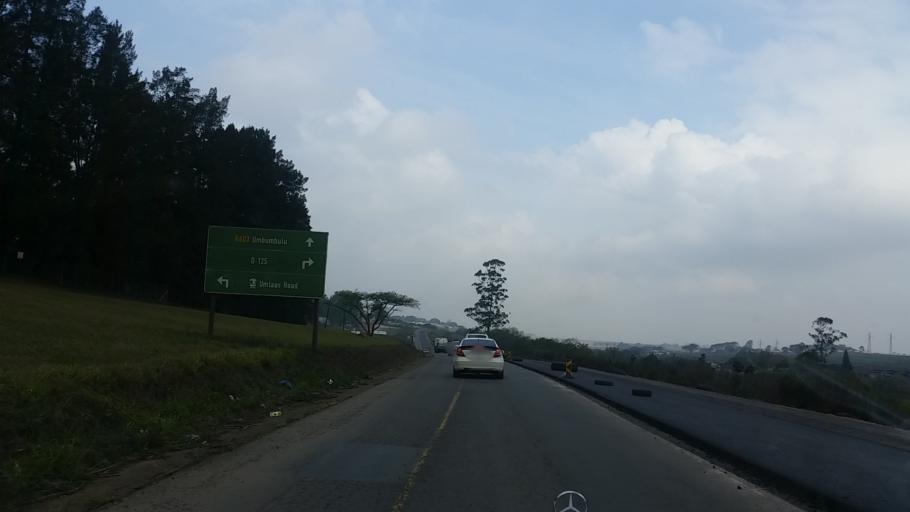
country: ZA
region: KwaZulu-Natal
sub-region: uMgungundlovu District Municipality
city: Camperdown
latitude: -29.7286
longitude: 30.5015
